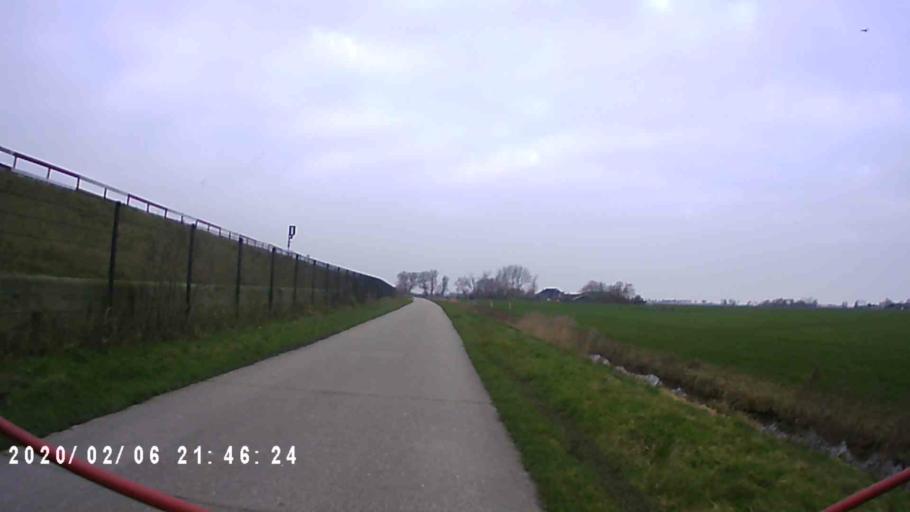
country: NL
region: Groningen
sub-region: Gemeente Zuidhorn
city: Noordhorn
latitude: 53.2549
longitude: 6.3847
